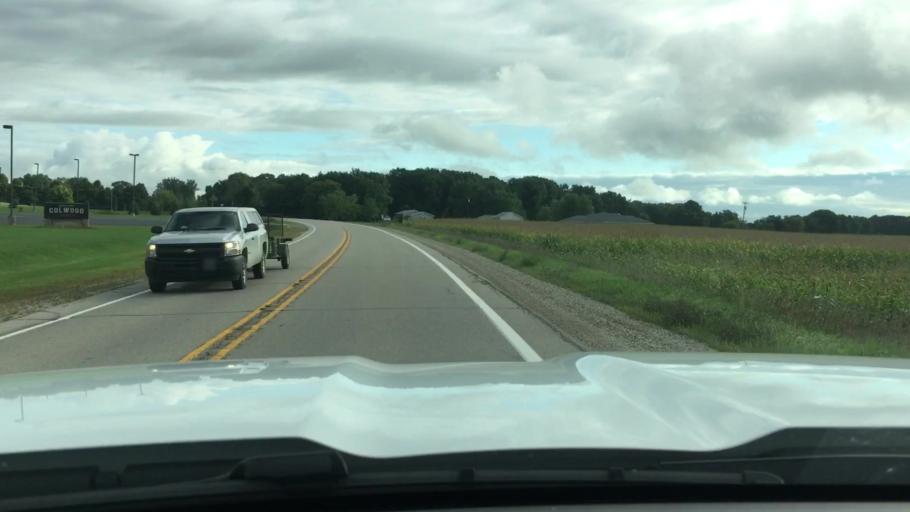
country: US
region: Michigan
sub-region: Tuscola County
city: Caro
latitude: 43.5253
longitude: -83.3485
